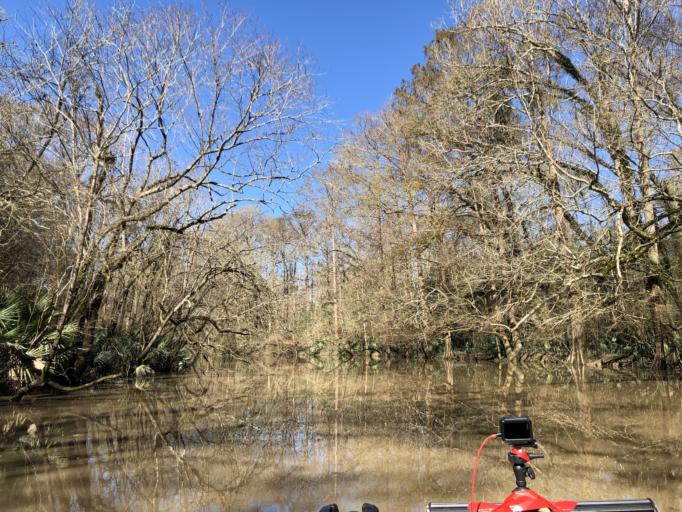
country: US
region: Louisiana
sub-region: Calcasieu Parish
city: Iowa
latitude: 30.3142
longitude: -93.0748
